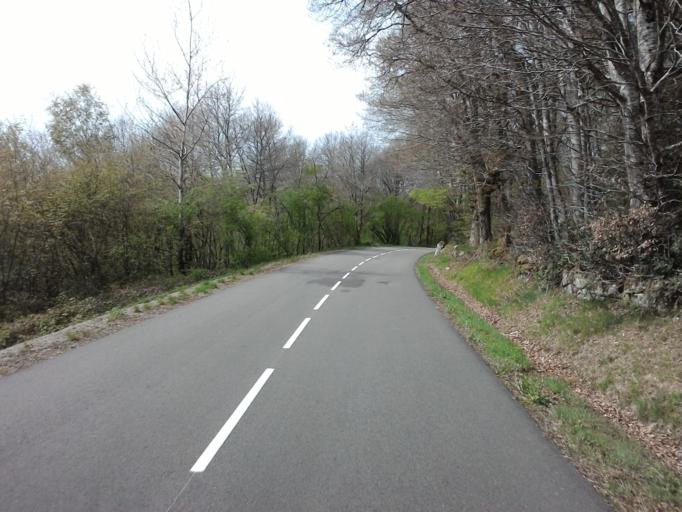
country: FR
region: Bourgogne
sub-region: Departement de la Cote-d'Or
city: Saulieu
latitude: 47.1809
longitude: 4.0873
